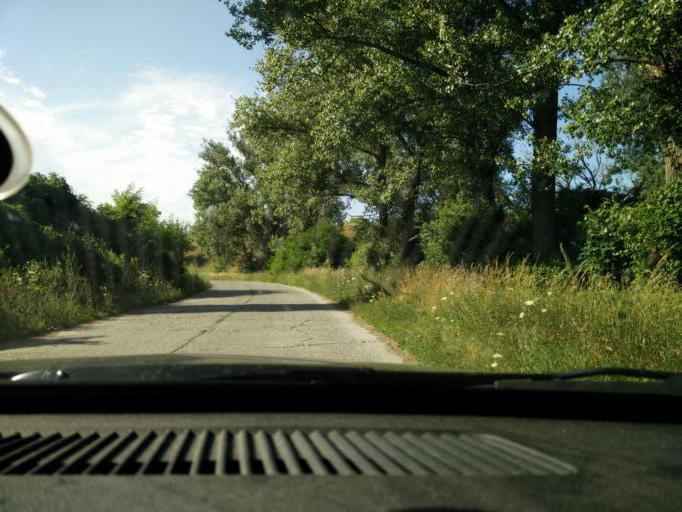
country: HU
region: Komarom-Esztergom
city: Tatabanya
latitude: 47.5600
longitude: 18.4466
